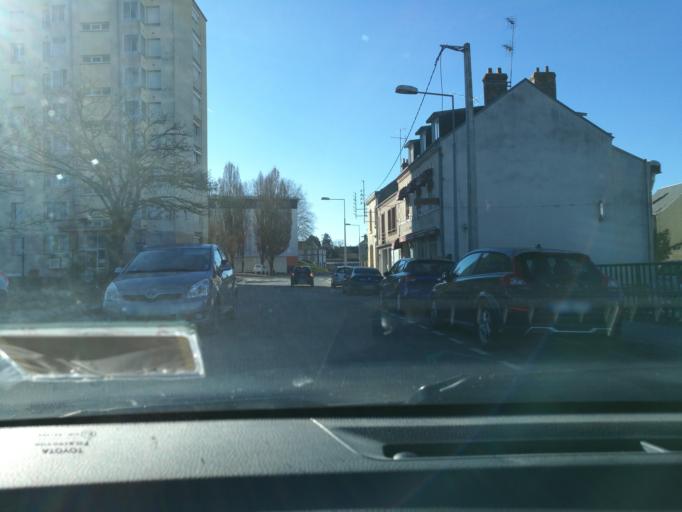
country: FR
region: Centre
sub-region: Departement du Loiret
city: Orleans
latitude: 47.9151
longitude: 1.9103
